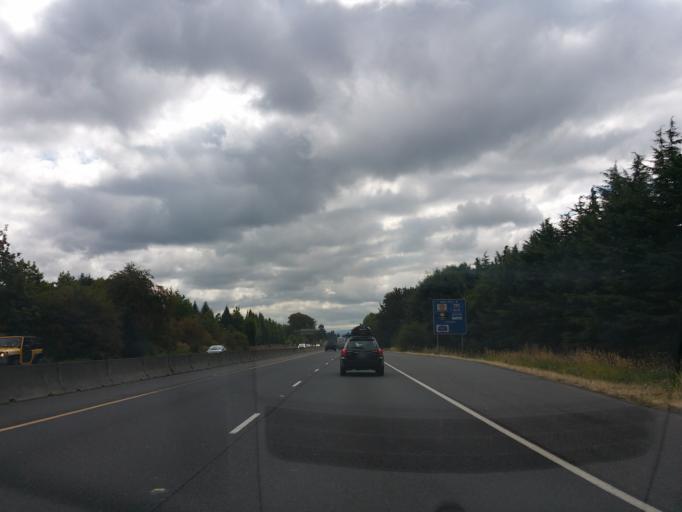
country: US
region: Washington
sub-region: Clark County
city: Mill Plain
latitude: 45.5972
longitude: -122.5239
